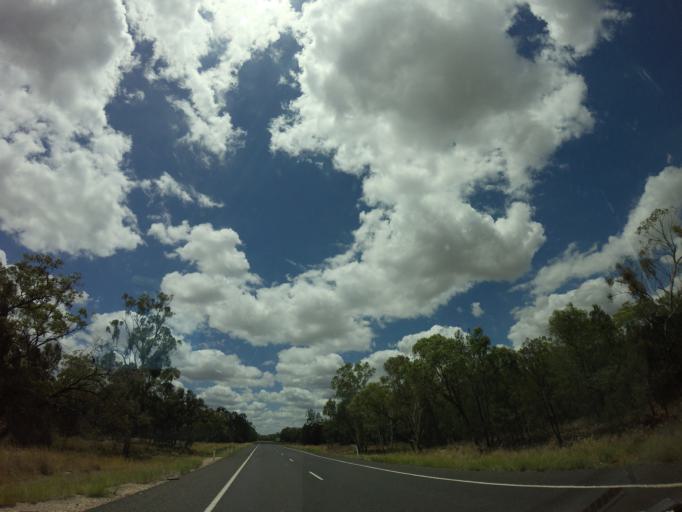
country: AU
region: Queensland
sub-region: Goondiwindi
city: Goondiwindi
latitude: -28.0999
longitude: 150.7246
